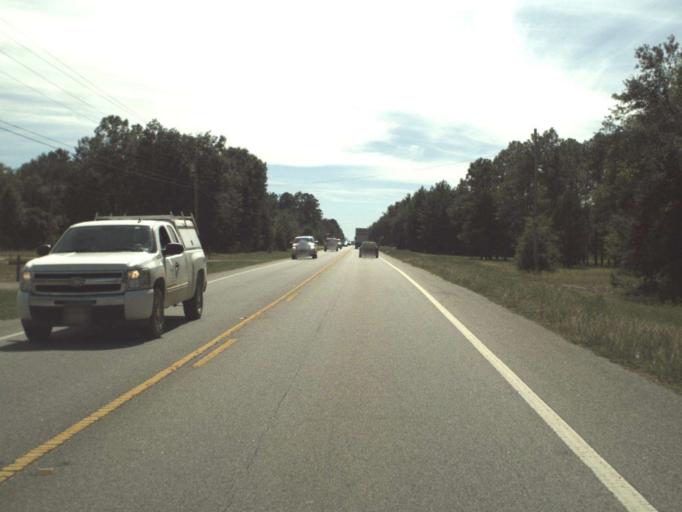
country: US
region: Florida
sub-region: Bay County
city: Lynn Haven
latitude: 30.5071
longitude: -85.6597
